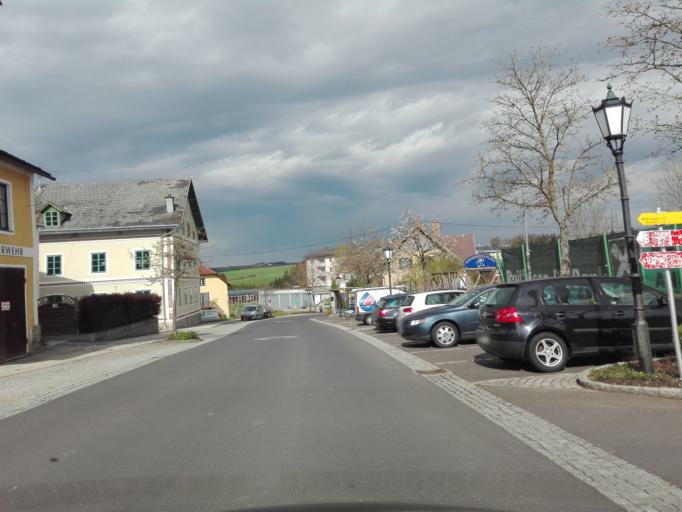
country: AT
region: Upper Austria
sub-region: Politischer Bezirk Rohrbach
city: Kleinzell im Muehlkreis
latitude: 48.4851
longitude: 14.0019
